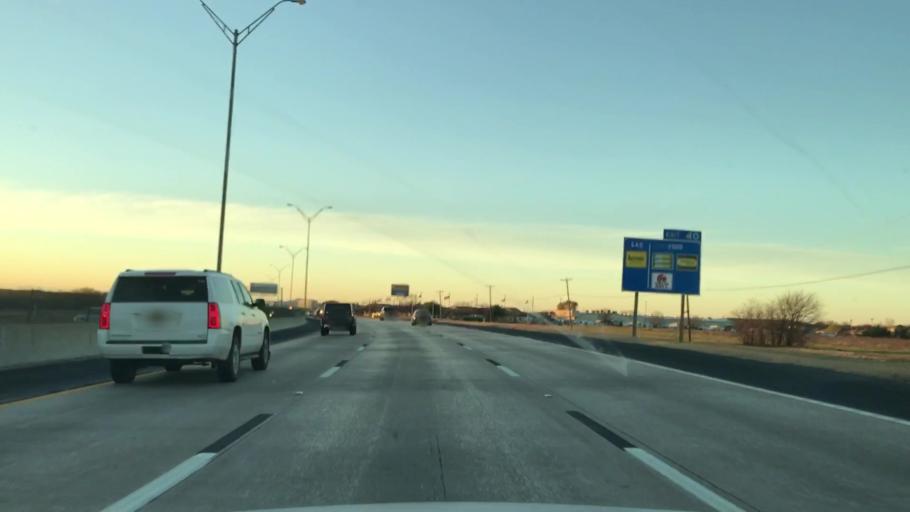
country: US
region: Texas
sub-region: Tarrant County
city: Everman
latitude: 32.6121
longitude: -97.3222
